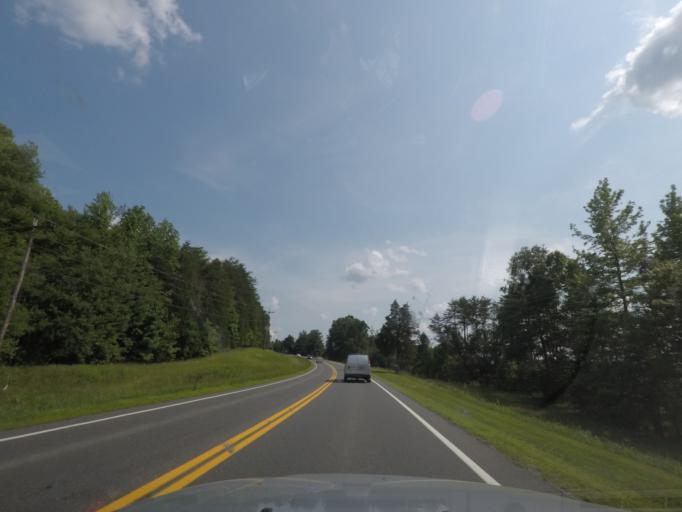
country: US
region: Virginia
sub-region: Fluvanna County
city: Palmyra
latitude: 37.8330
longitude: -78.2740
